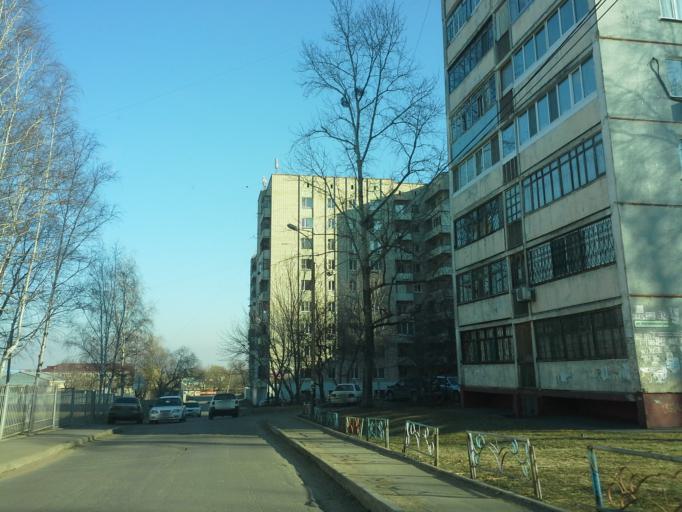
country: RU
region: Khabarovsk Krai
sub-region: Khabarovskiy Rayon
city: Khabarovsk
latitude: 48.4806
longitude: 135.1203
